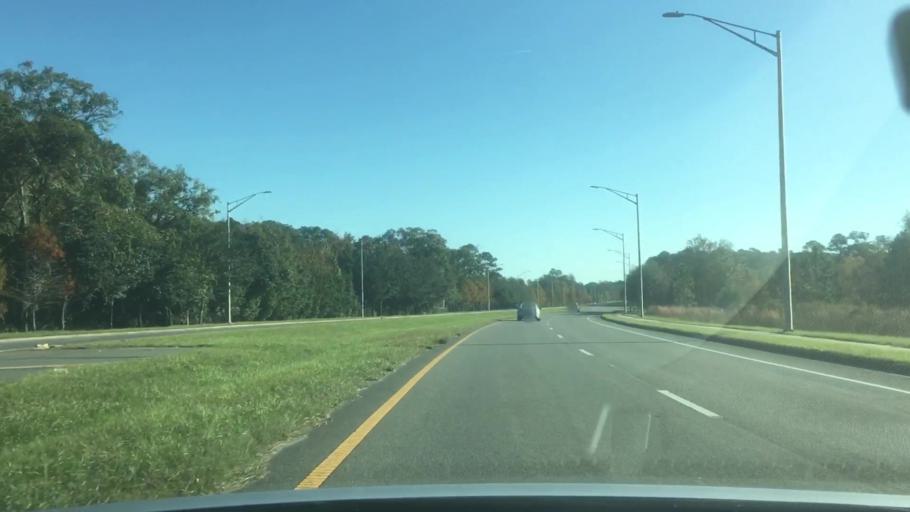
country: US
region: Florida
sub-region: Duval County
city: Jacksonville
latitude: 30.4758
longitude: -81.6251
